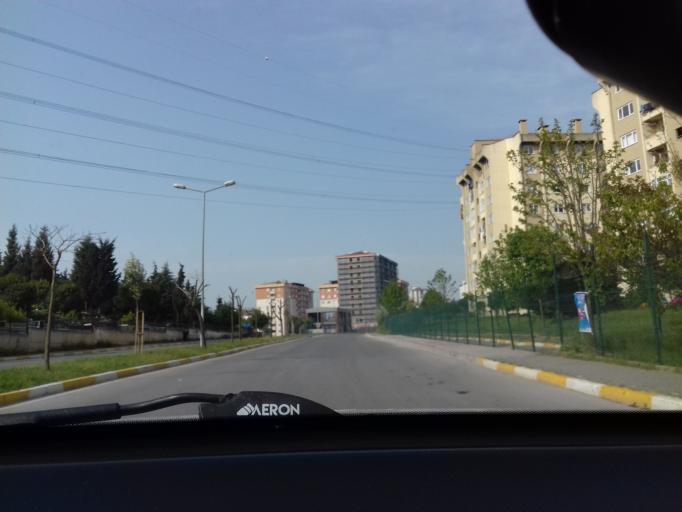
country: TR
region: Istanbul
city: Pendik
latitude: 40.9089
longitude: 29.2757
